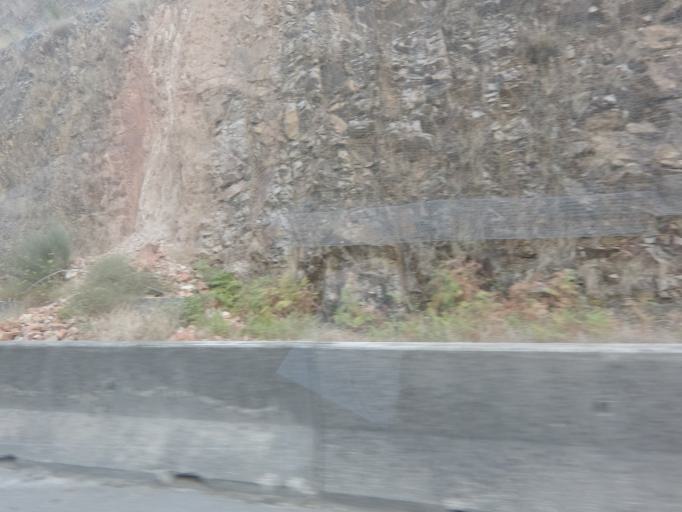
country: PT
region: Coimbra
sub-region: Penacova
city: Penacova
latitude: 40.2840
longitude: -8.2634
